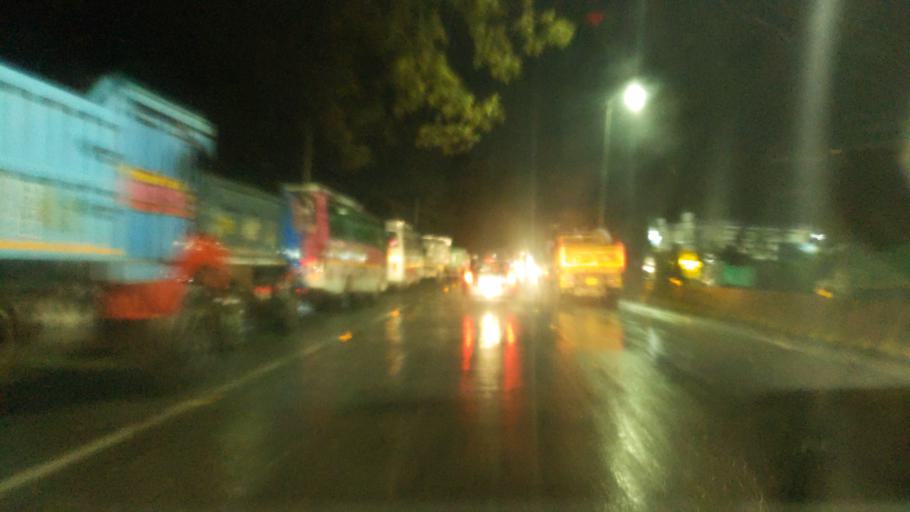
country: IN
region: Uttarakhand
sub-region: Naini Tal
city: Haldwani
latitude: 29.2488
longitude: 79.5392
